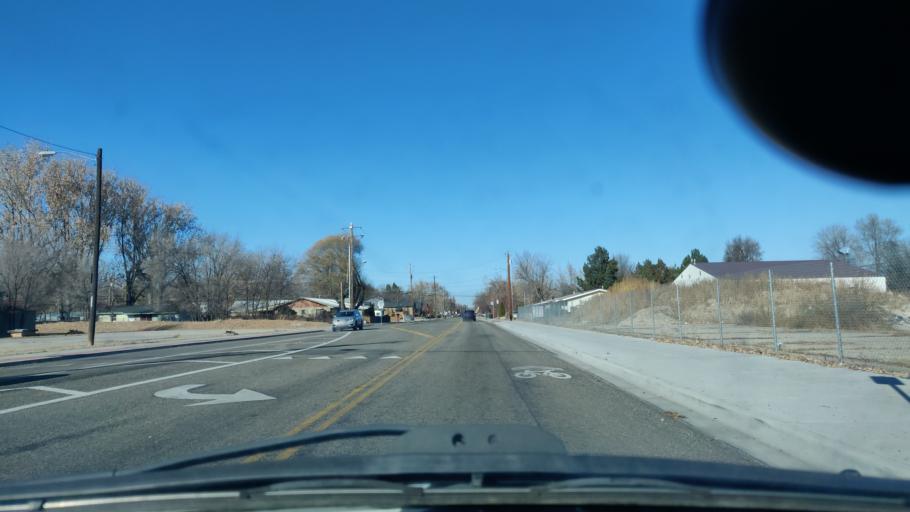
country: US
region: Idaho
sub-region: Ada County
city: Garden City
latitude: 43.6345
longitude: -116.2470
